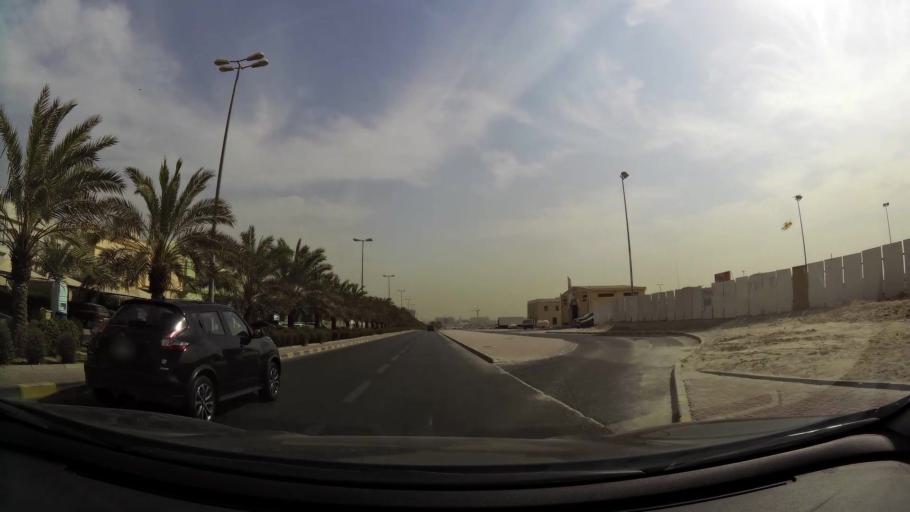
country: KW
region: Al Farwaniyah
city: Janub as Surrah
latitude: 29.2716
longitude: 48.0031
